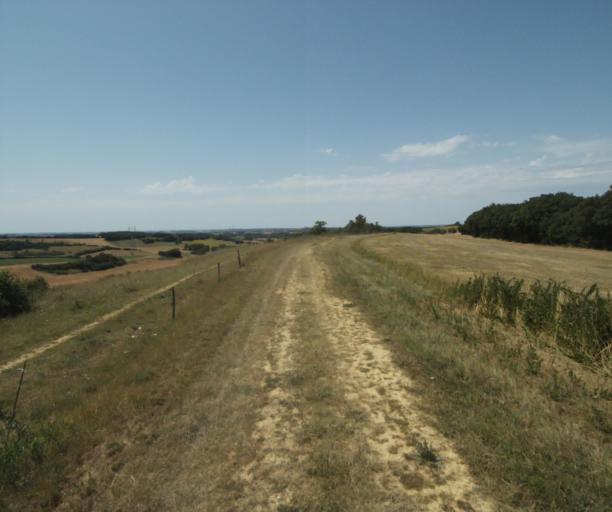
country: FR
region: Midi-Pyrenees
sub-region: Departement de la Haute-Garonne
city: Saint-Felix-Lauragais
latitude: 43.4416
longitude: 1.8687
